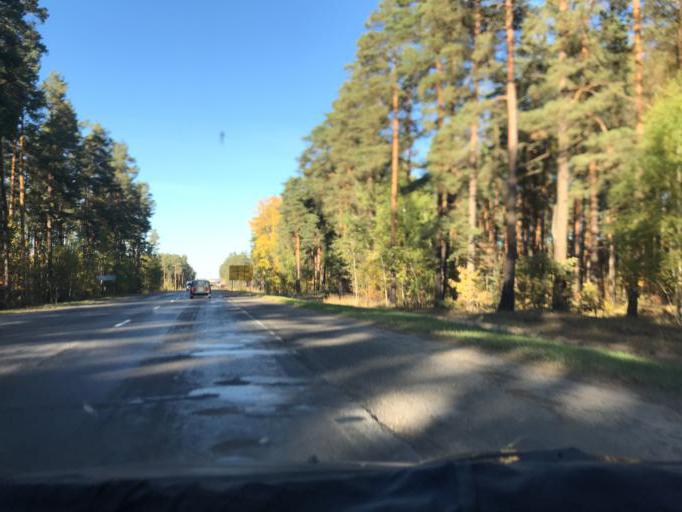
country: BY
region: Gomel
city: Kalinkavichy
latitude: 52.0620
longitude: 29.3610
